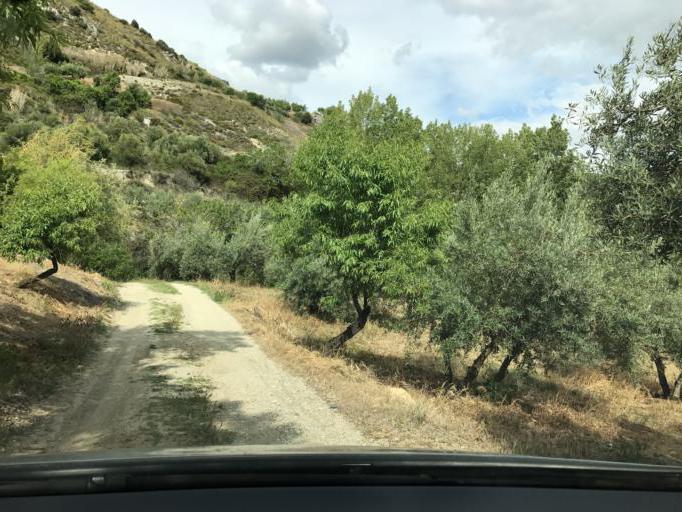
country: ES
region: Andalusia
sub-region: Provincia de Granada
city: Beas de Granada
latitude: 37.2194
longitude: -3.4548
